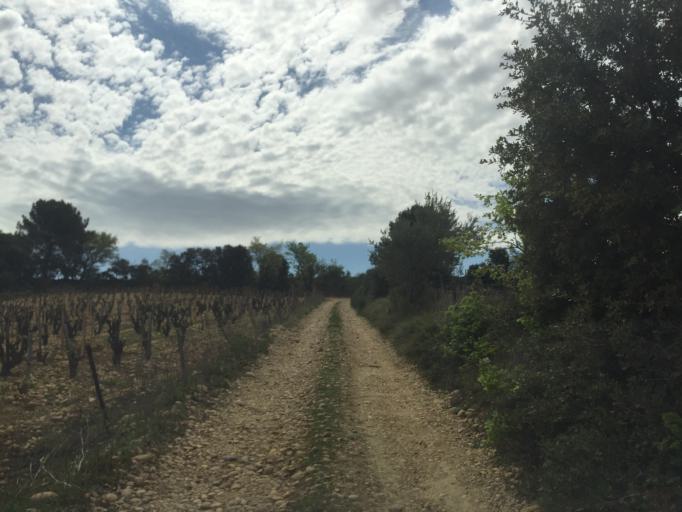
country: FR
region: Provence-Alpes-Cote d'Azur
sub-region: Departement du Vaucluse
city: Chateauneuf-du-Pape
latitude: 44.0635
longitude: 4.8530
